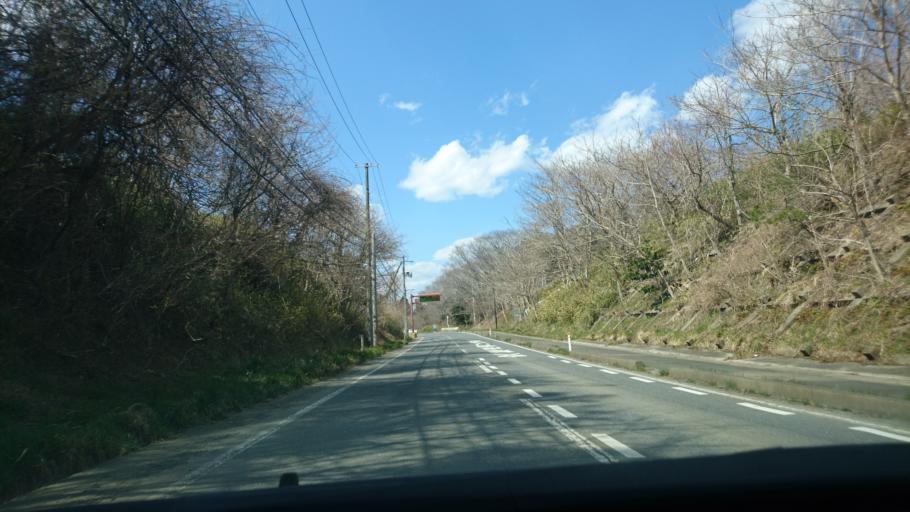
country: JP
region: Miyagi
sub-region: Oshika Gun
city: Onagawa Cho
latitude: 38.6380
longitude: 141.4989
